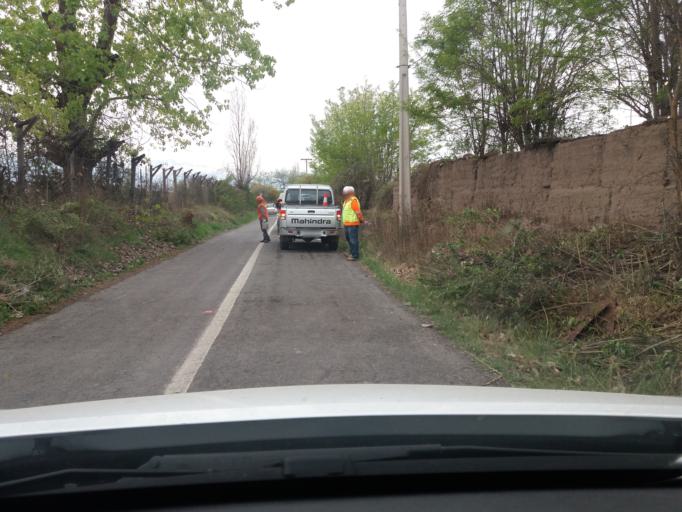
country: CL
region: Valparaiso
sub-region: Provincia de Los Andes
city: Los Andes
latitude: -32.8246
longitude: -70.6419
